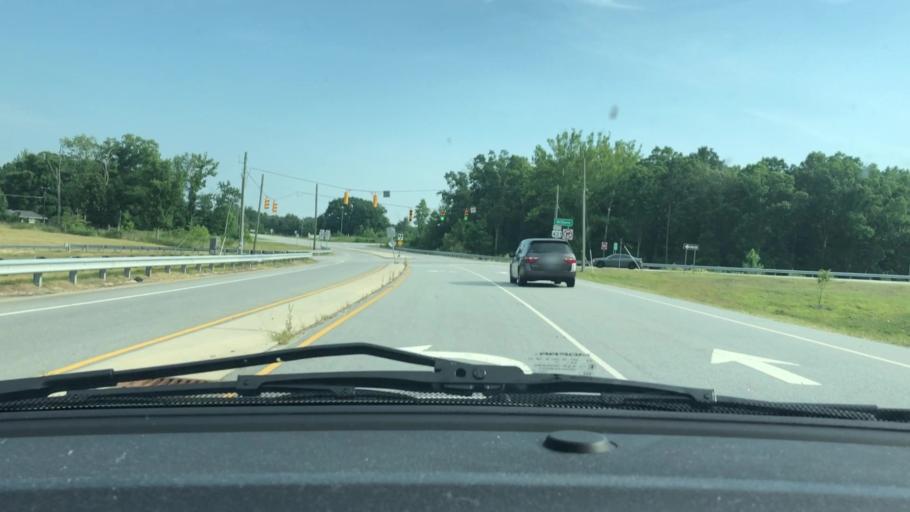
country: US
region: North Carolina
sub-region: Guilford County
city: Forest Oaks
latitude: 35.9626
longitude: -79.7038
